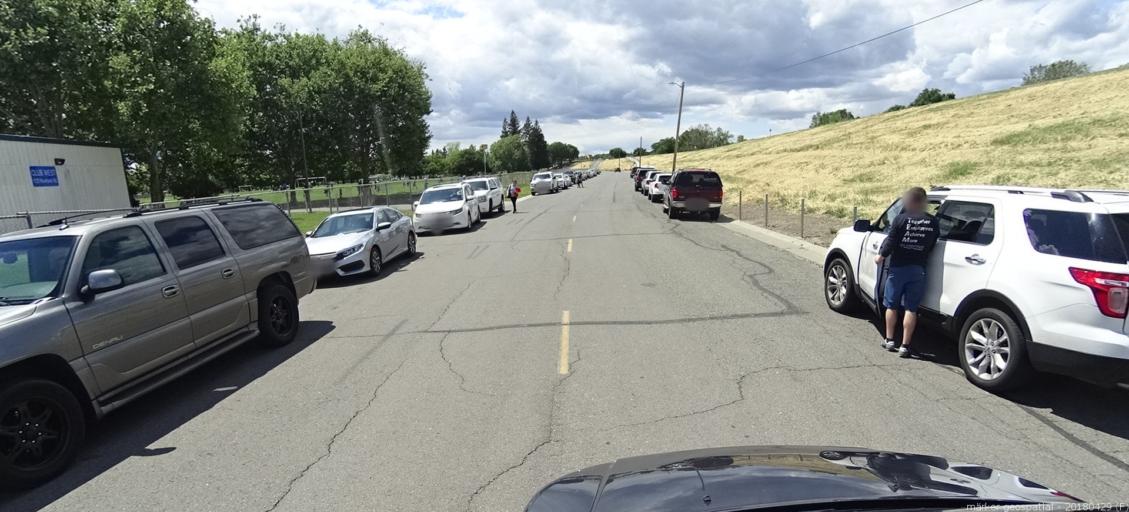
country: US
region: California
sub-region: Yolo County
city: West Sacramento
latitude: 38.6019
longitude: -121.5319
